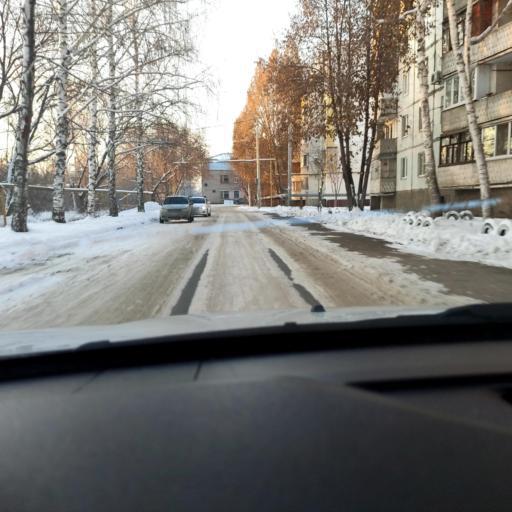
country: RU
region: Samara
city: Smyshlyayevka
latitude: 53.2514
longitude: 50.3752
